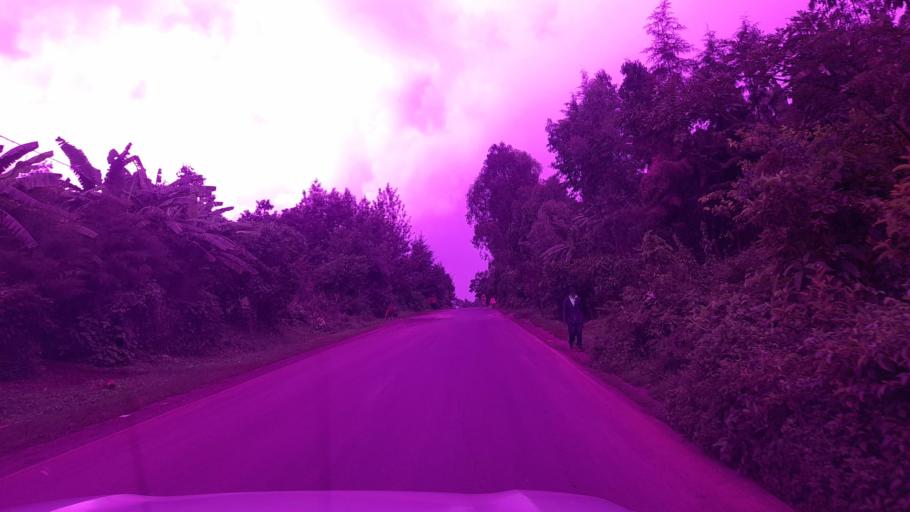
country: ET
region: Oromiya
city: Jima
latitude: 7.6645
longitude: 36.8897
